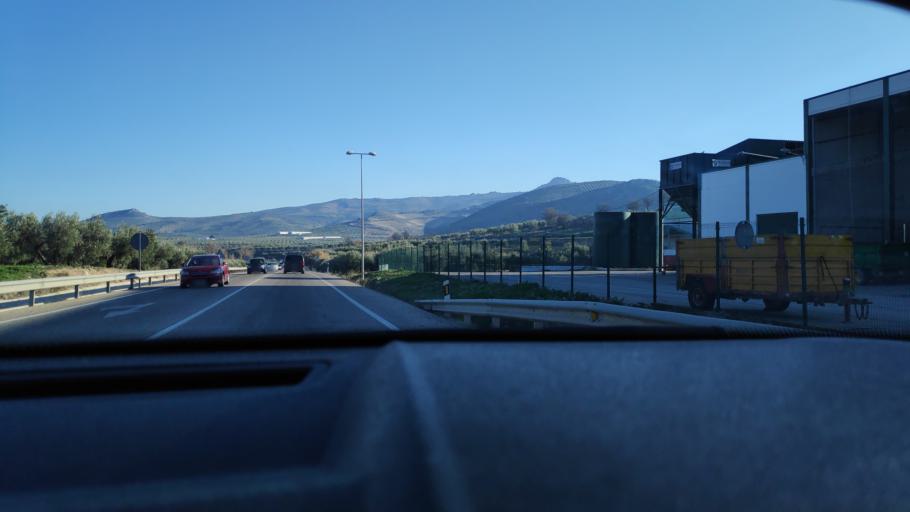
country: ES
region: Andalusia
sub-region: Province of Cordoba
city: Luque
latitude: 37.5709
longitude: -4.2524
